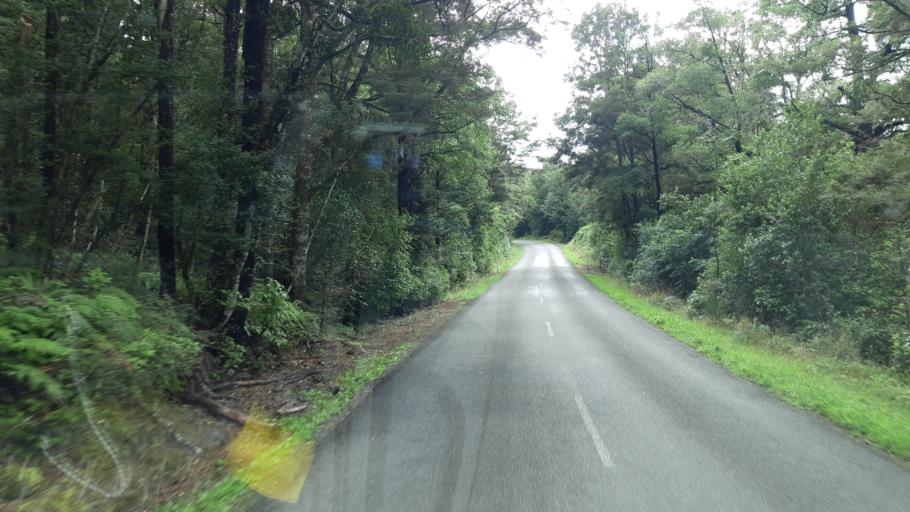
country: NZ
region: West Coast
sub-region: Buller District
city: Westport
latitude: -41.7853
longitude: 172.3678
